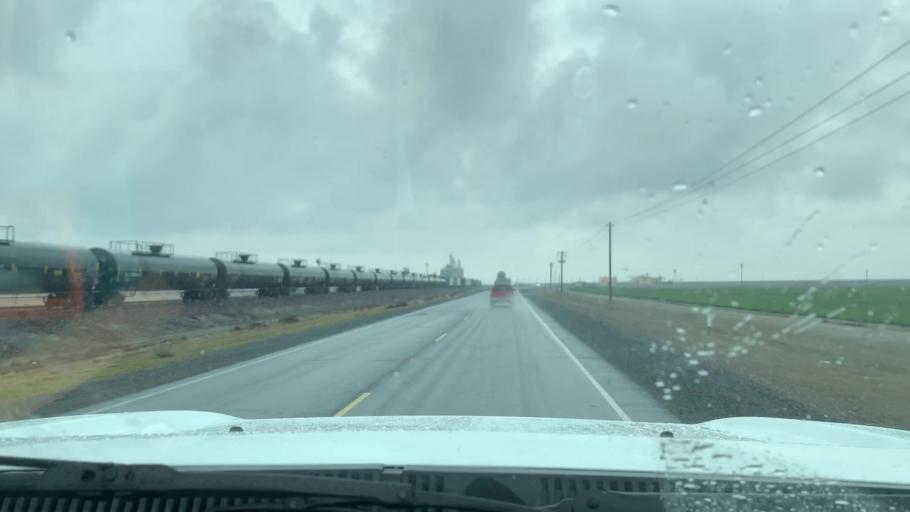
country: US
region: California
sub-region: Tulare County
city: Alpaugh
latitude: 35.9820
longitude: -119.4714
